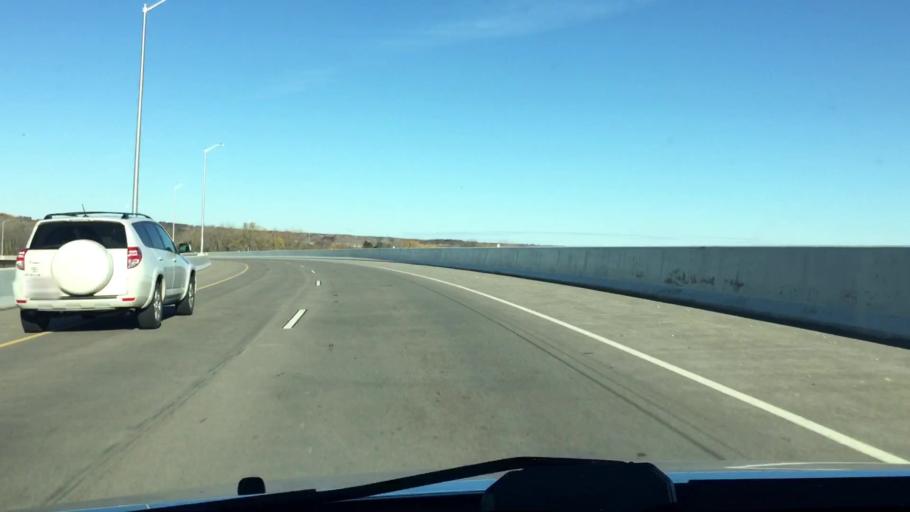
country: US
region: Wisconsin
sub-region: Brown County
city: Howard
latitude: 44.5385
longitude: -88.0788
